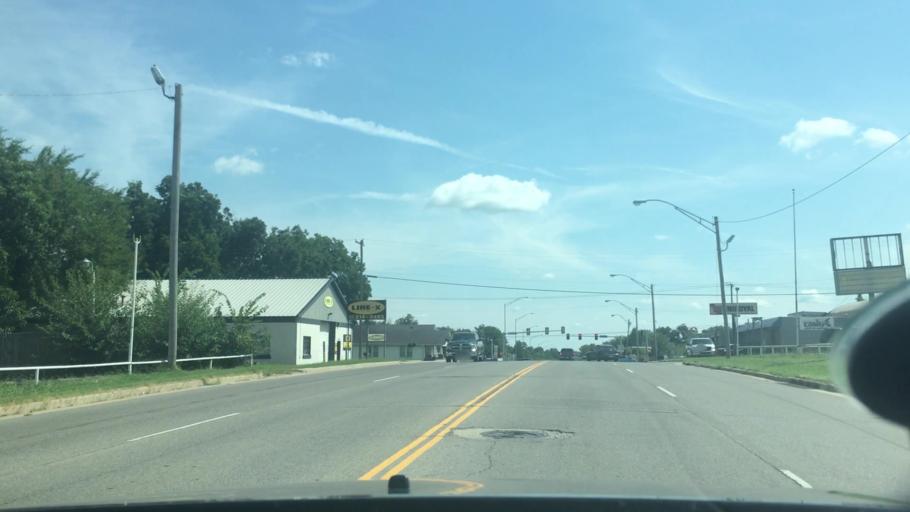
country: US
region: Oklahoma
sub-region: Pottawatomie County
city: Shawnee
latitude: 35.3344
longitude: -96.9121
